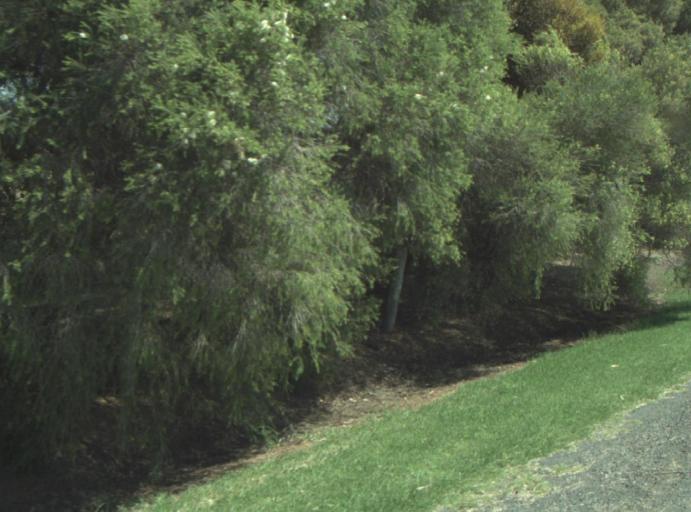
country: AU
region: Victoria
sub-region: Greater Geelong
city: Leopold
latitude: -38.1704
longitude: 144.4542
